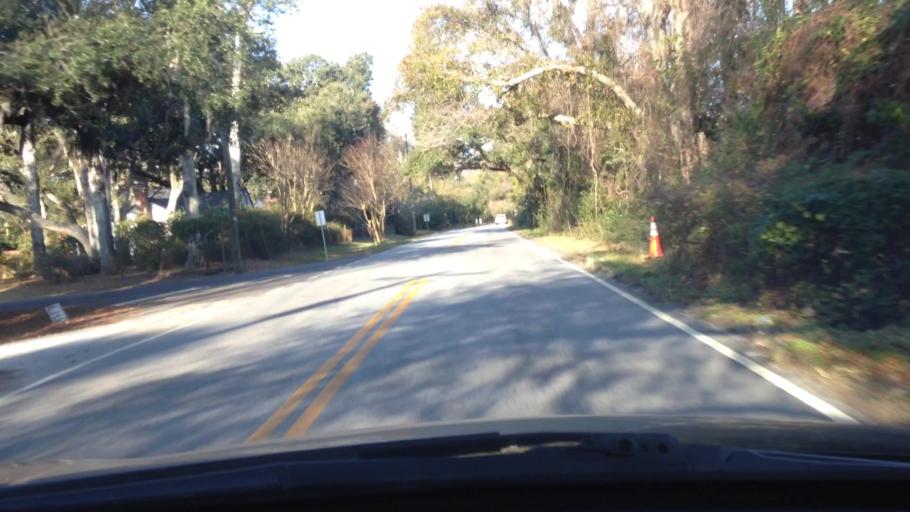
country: US
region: South Carolina
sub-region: Charleston County
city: Charleston
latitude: 32.7522
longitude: -79.9935
